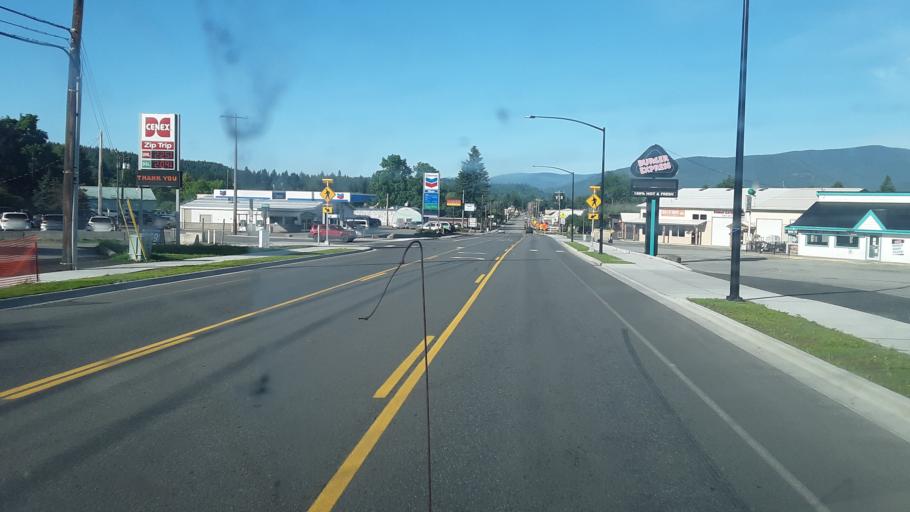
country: US
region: Idaho
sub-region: Boundary County
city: Bonners Ferry
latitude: 48.6844
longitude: -116.3208
